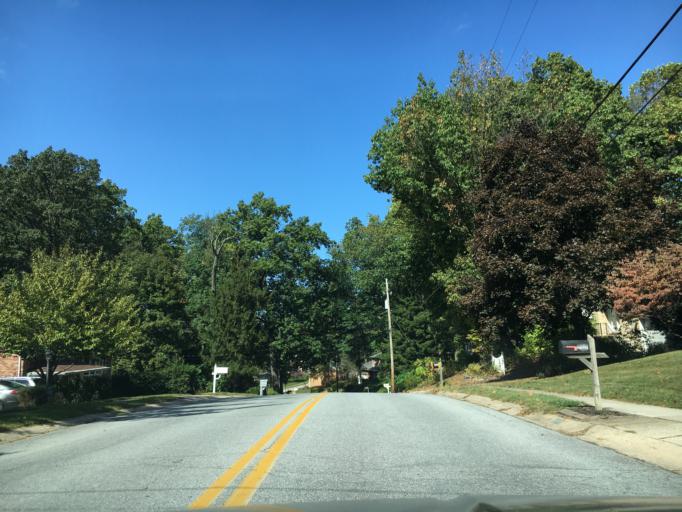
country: US
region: Pennsylvania
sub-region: York County
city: East York
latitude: 39.9611
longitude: -76.6683
